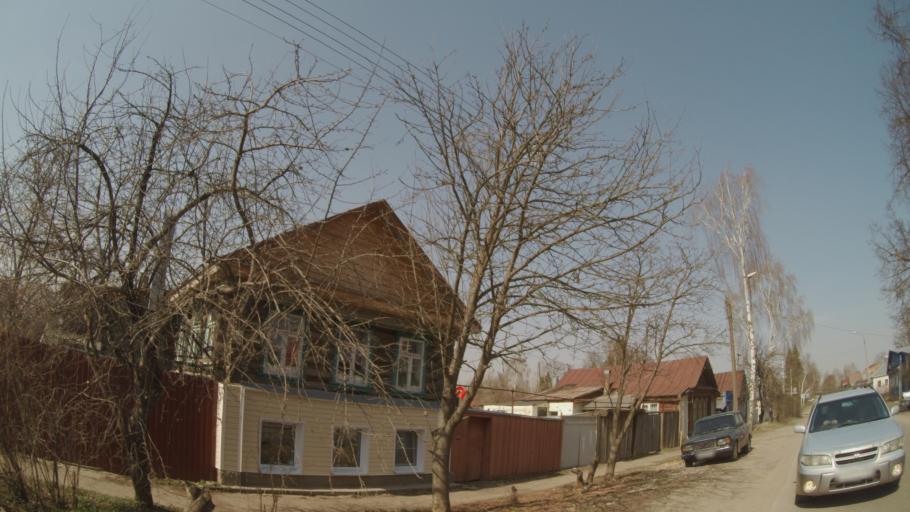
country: RU
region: Nizjnij Novgorod
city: Arzamas
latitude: 55.3882
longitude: 43.8244
